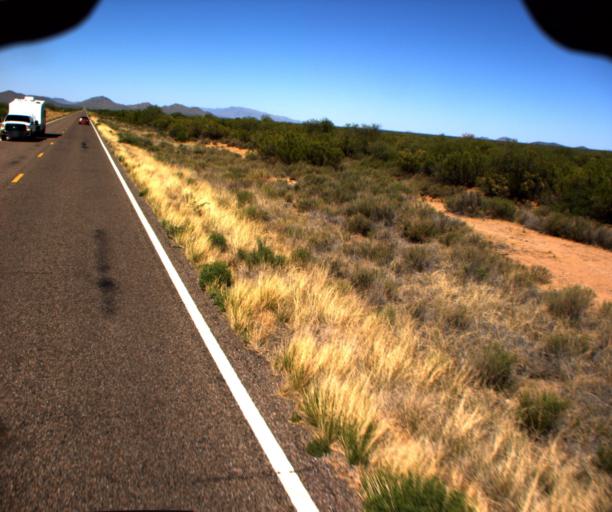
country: US
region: Arizona
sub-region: Yavapai County
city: Congress
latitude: 34.1470
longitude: -112.8911
